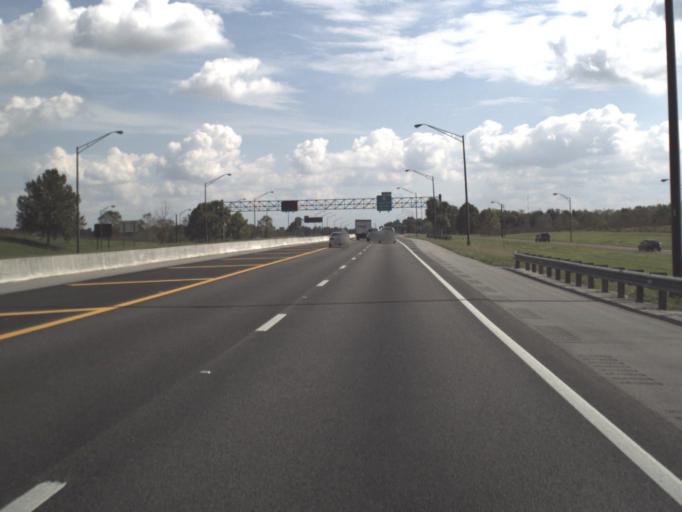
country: US
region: Florida
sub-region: Polk County
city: Crystal Lake
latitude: 27.9964
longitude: -81.9214
